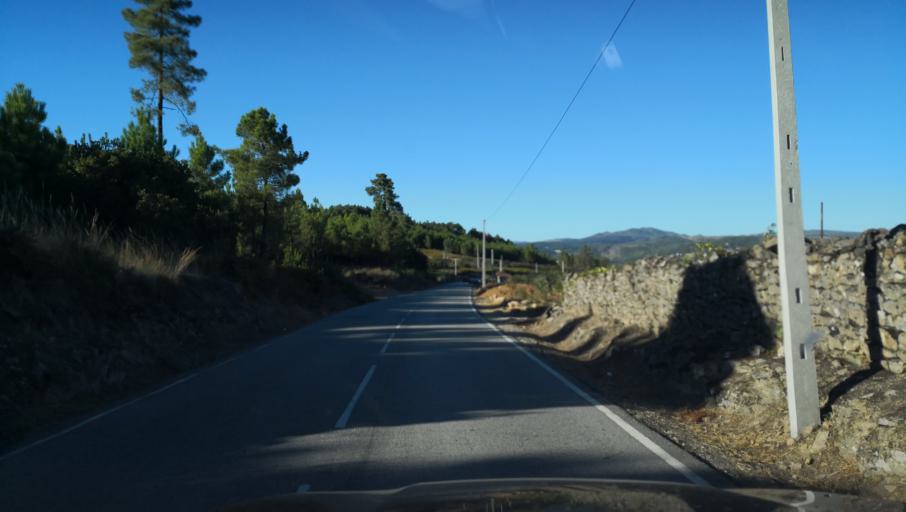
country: PT
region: Vila Real
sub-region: Sabrosa
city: Sabrosa
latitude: 41.2837
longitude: -7.5764
